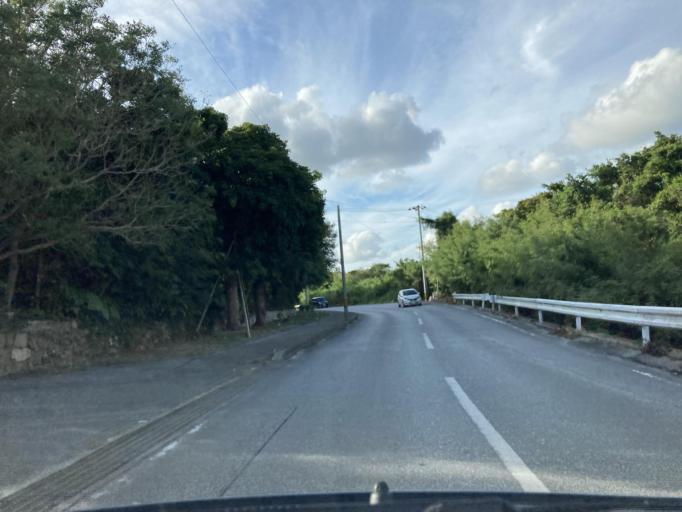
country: JP
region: Okinawa
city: Itoman
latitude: 26.1333
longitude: 127.7524
